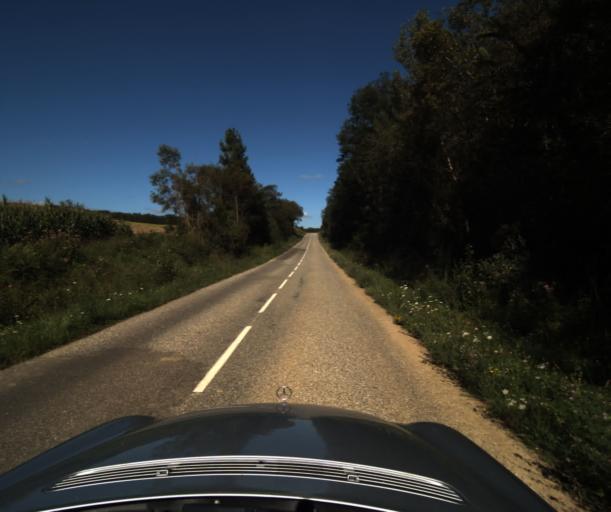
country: FR
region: Midi-Pyrenees
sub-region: Departement de l'Ariege
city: Belesta
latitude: 42.9705
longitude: 1.9310
